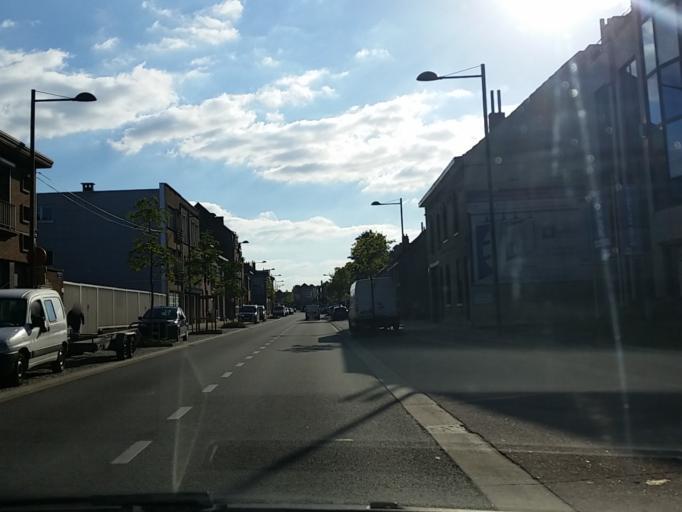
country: BE
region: Flanders
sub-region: Provincie Vlaams-Brabant
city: Diegem
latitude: 50.8898
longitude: 4.4261
